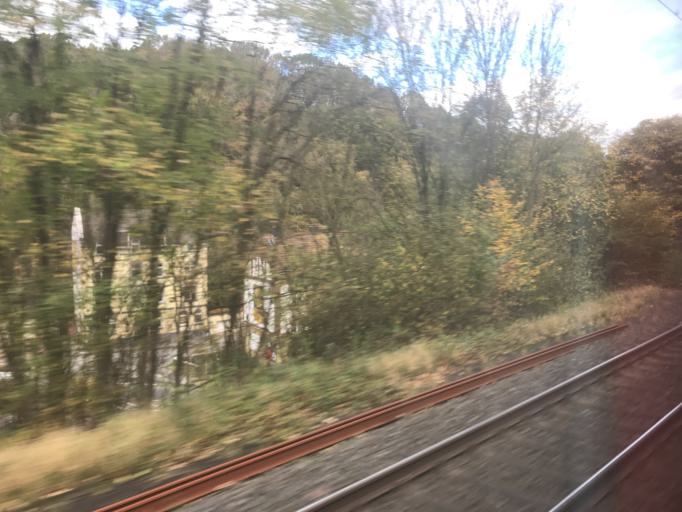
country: DE
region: North Rhine-Westphalia
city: Gevelsberg
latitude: 51.2969
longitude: 7.3344
